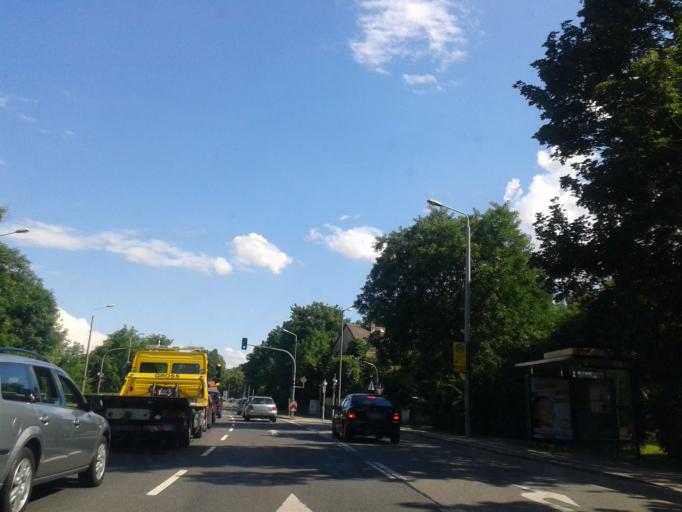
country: DE
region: Saxony
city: Radebeul
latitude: 51.0677
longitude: 13.6739
